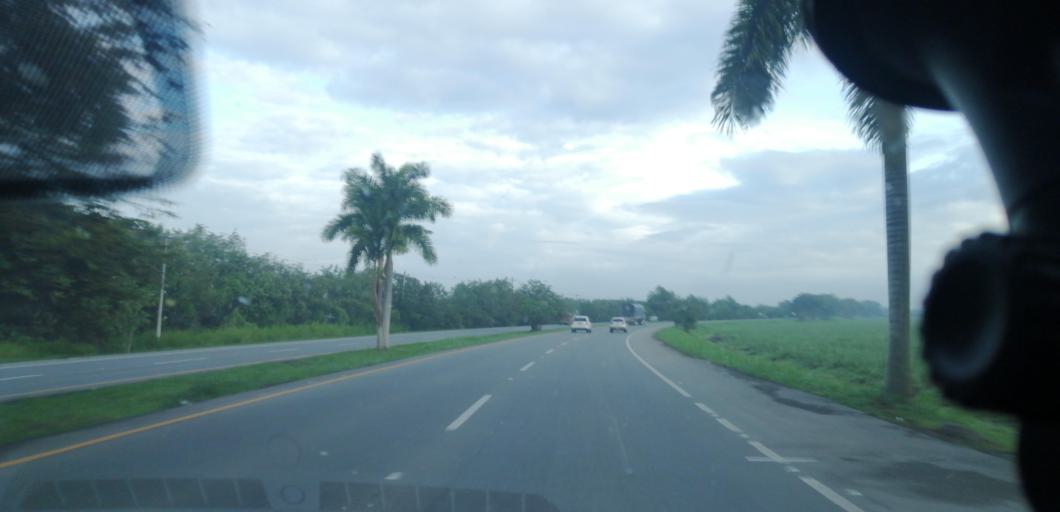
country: CO
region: Valle del Cauca
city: Palmira
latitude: 3.5461
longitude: -76.3382
